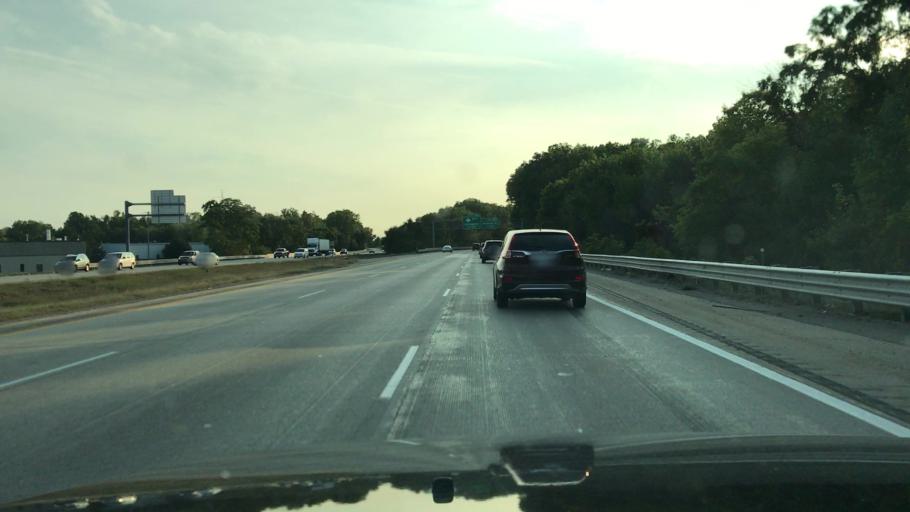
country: US
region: Michigan
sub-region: Kent County
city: Grandville
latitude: 42.9112
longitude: -85.7704
